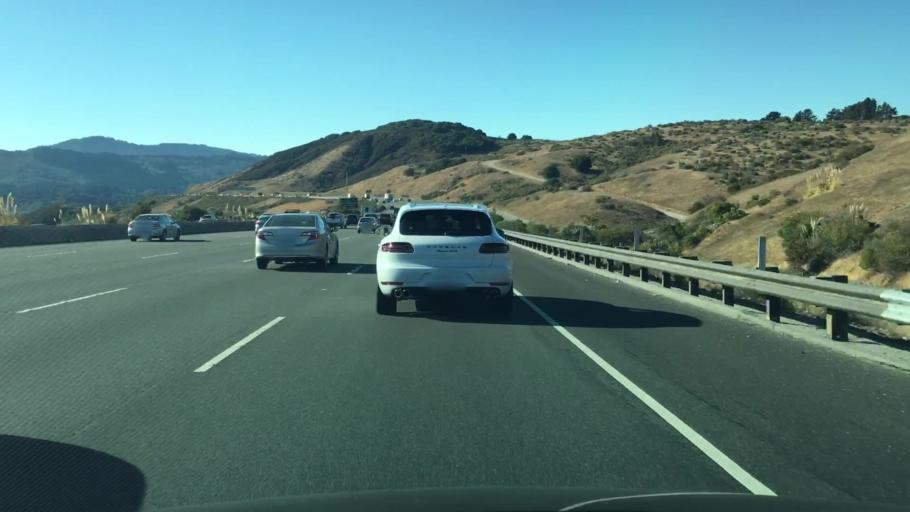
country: US
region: California
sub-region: San Mateo County
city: Highlands-Baywood Park
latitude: 37.4976
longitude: -122.3140
